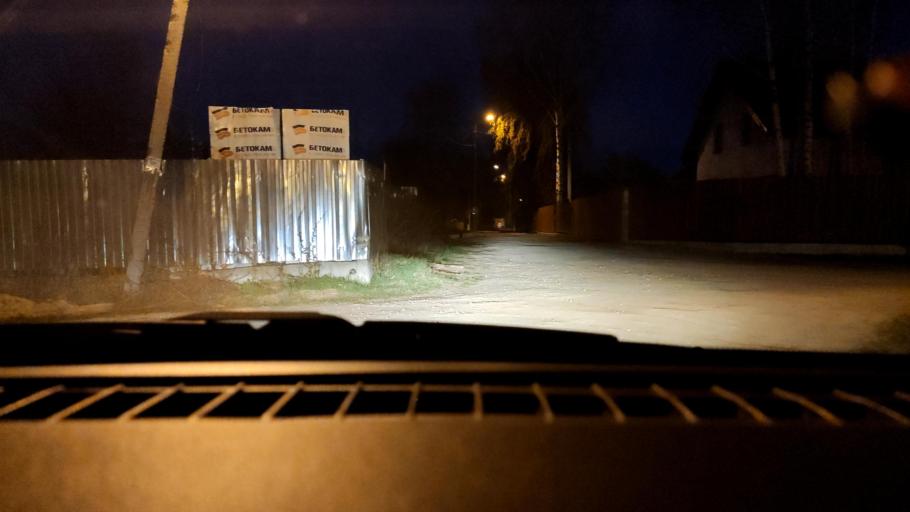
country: RU
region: Perm
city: Perm
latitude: 58.0295
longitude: 56.2052
